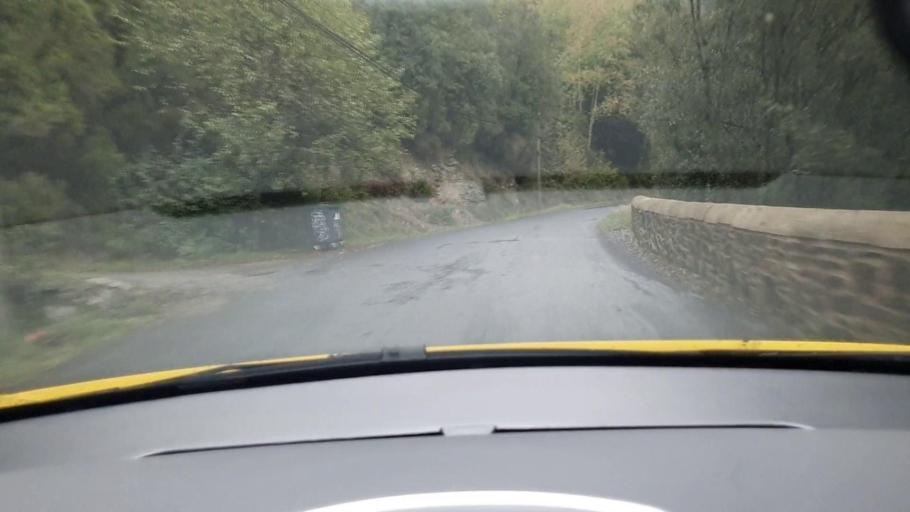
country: FR
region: Languedoc-Roussillon
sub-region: Departement du Gard
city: Sumene
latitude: 44.0004
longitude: 3.7107
